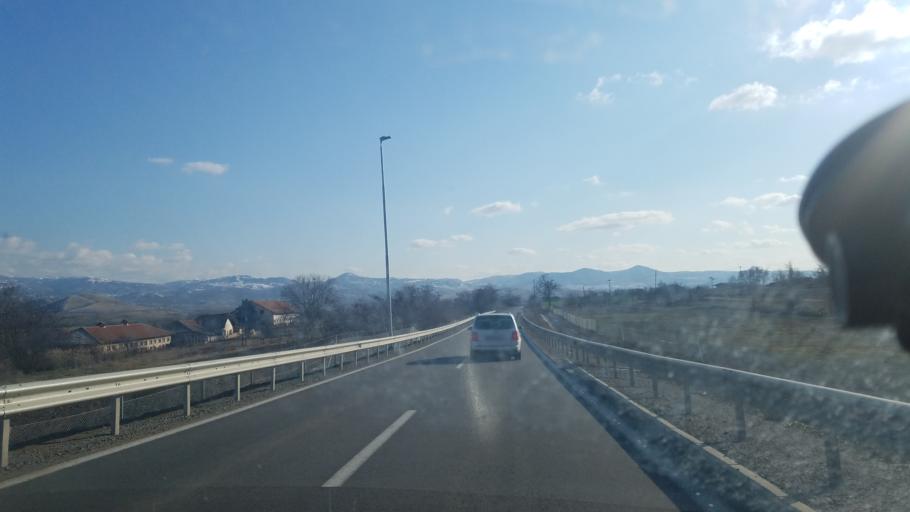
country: MK
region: Karbinci
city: Karbinci
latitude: 41.8582
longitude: 22.2381
